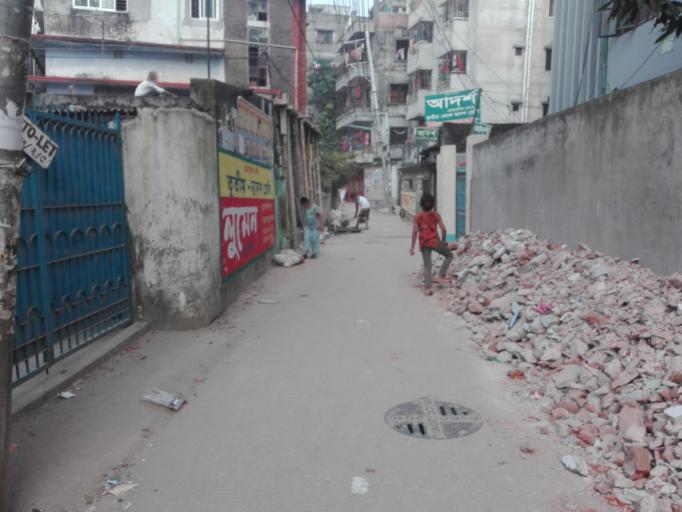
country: BD
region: Dhaka
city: Azimpur
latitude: 23.7935
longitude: 90.3581
